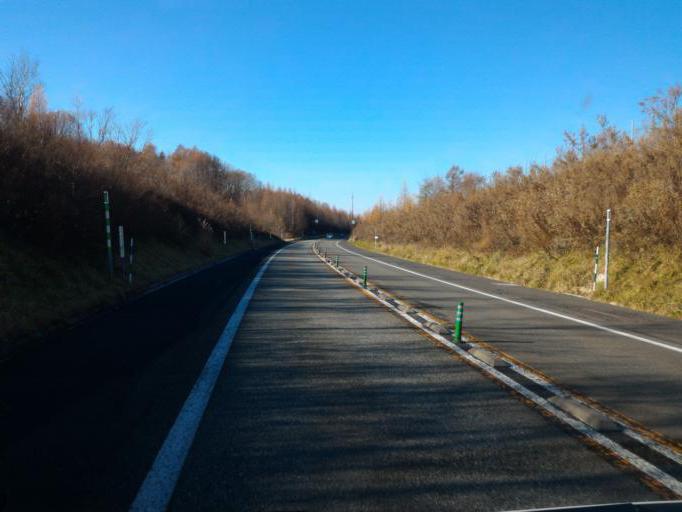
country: JP
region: Hokkaido
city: Chitose
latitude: 42.8957
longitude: 141.8614
